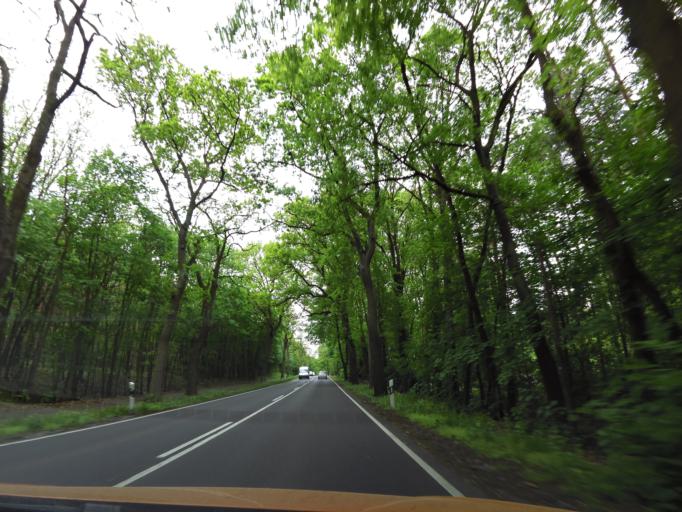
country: DE
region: Brandenburg
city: Beelitz
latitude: 52.2688
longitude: 12.9987
